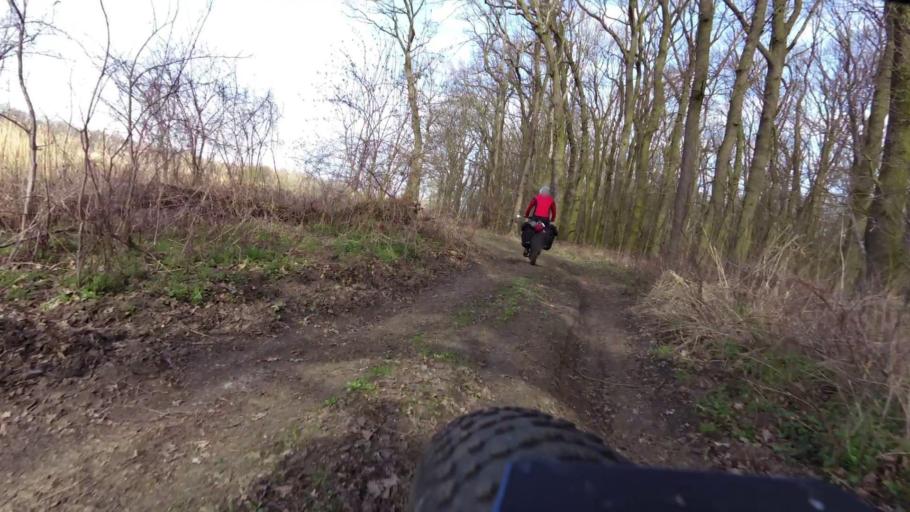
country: PL
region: Lubusz
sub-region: Powiat slubicki
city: Slubice
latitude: 52.3284
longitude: 14.5649
